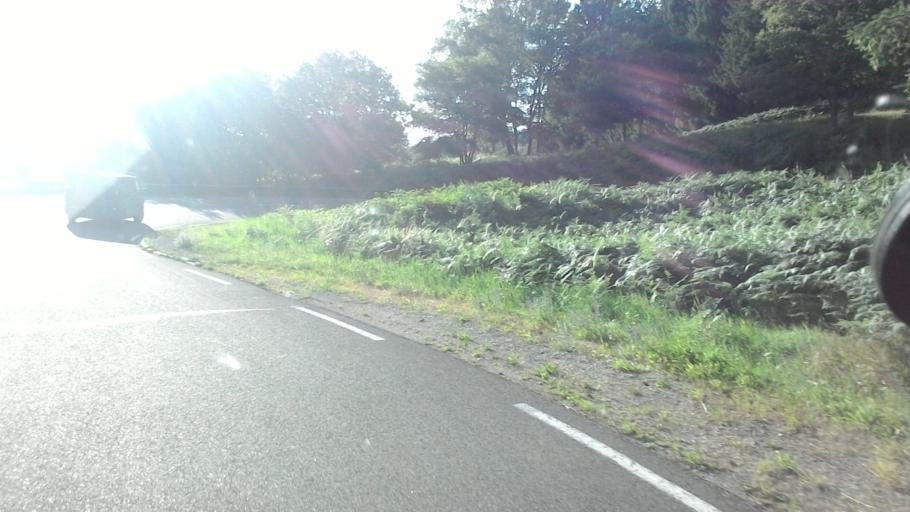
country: FR
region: Lorraine
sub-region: Departement des Vosges
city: Rupt-sur-Moselle
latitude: 47.8981
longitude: 6.6368
